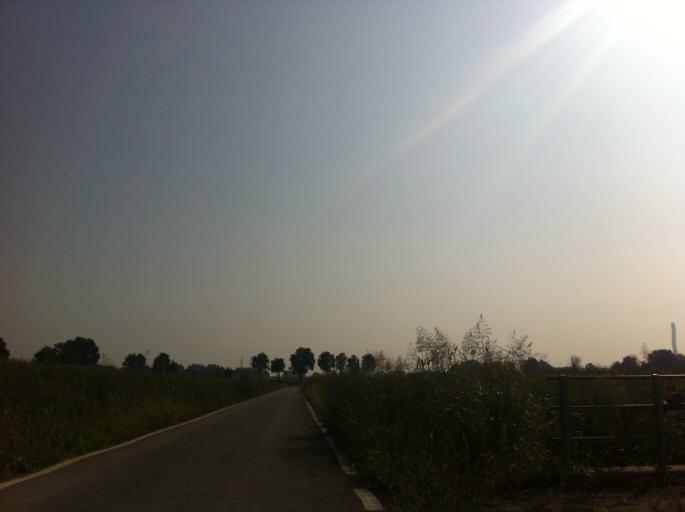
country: IT
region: Lombardy
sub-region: Provincia di Lodi
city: Tavazzano
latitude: 45.3431
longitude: 9.3984
